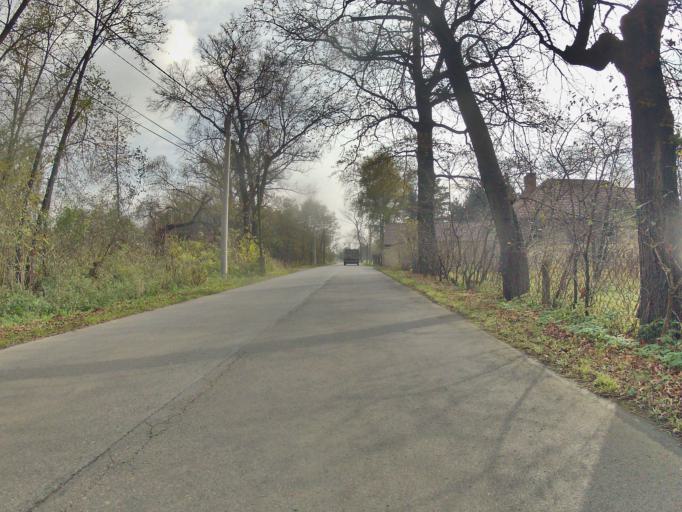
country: PL
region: Lesser Poland Voivodeship
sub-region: Powiat wielicki
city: Wegrzce Wielkie
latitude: 50.0600
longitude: 20.1094
